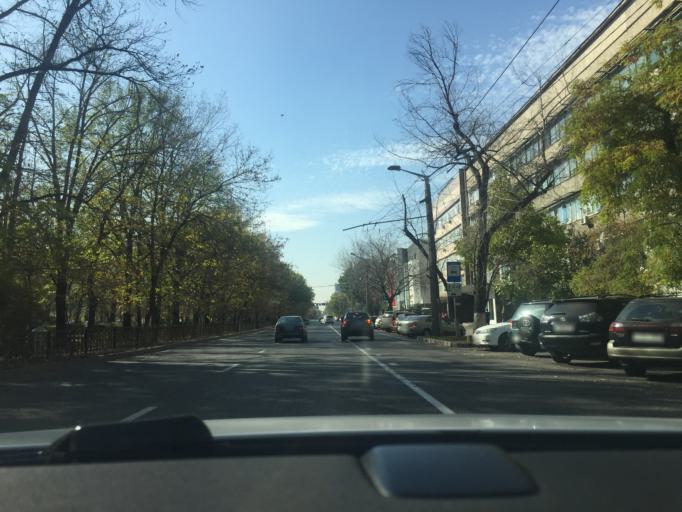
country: KZ
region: Almaty Qalasy
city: Almaty
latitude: 43.2398
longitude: 76.9031
